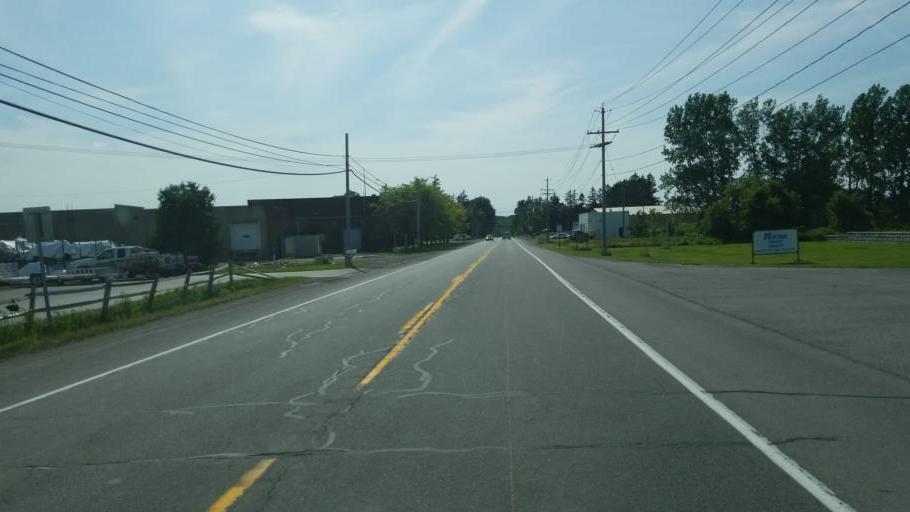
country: US
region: New York
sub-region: Livingston County
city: Lima
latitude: 42.9086
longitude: -77.5949
